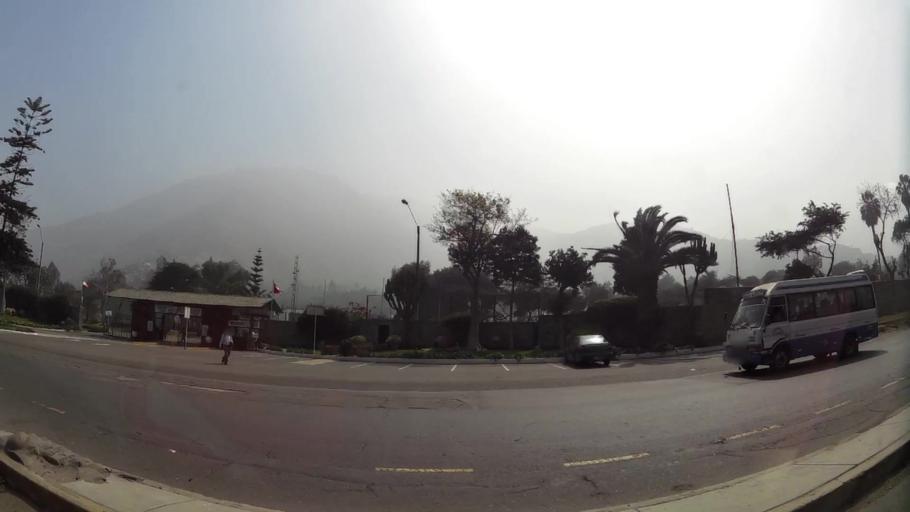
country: PE
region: Lima
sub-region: Lima
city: Chosica
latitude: -11.9548
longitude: -76.7306
